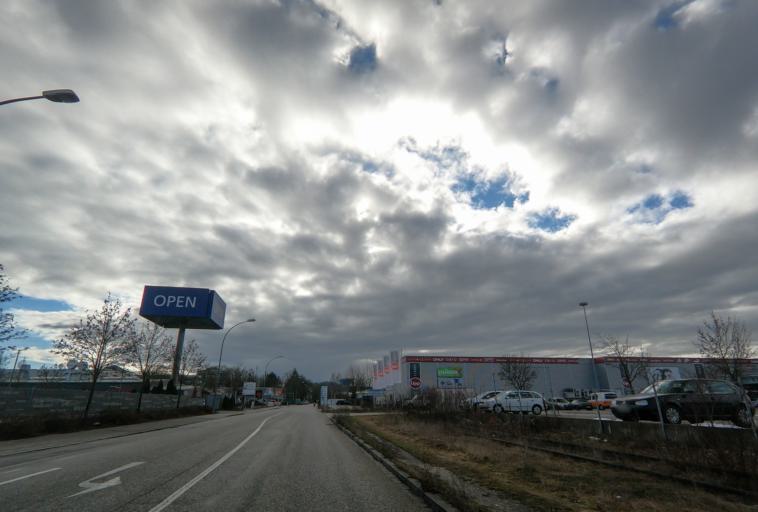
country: DE
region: Bavaria
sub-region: Lower Bavaria
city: Landshut
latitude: 48.5542
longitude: 12.1507
